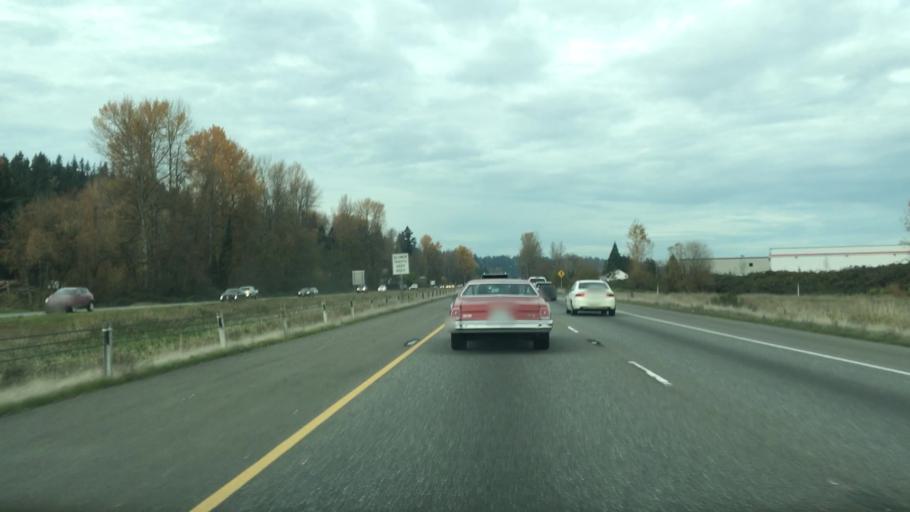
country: US
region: Washington
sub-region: King County
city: Pacific
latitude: 47.2374
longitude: -122.2525
